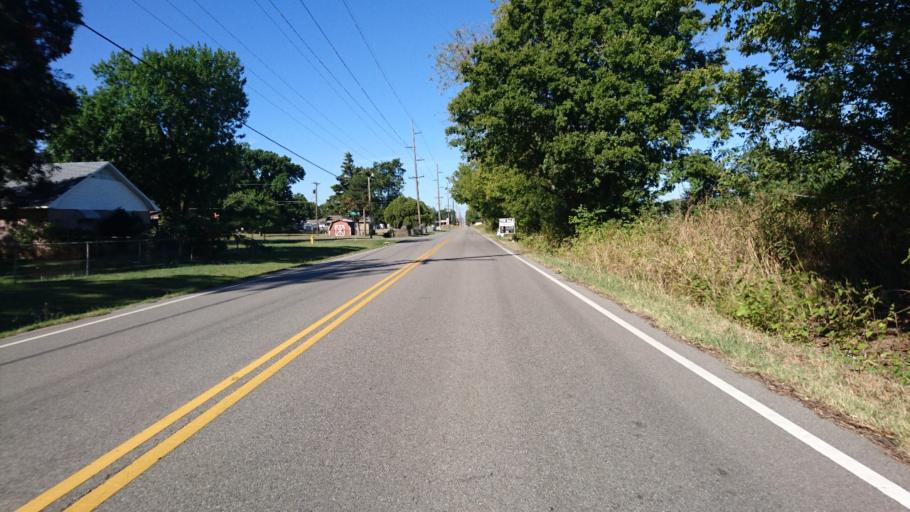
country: US
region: Oklahoma
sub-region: Rogers County
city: Catoosa
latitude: 36.1480
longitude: -95.8103
